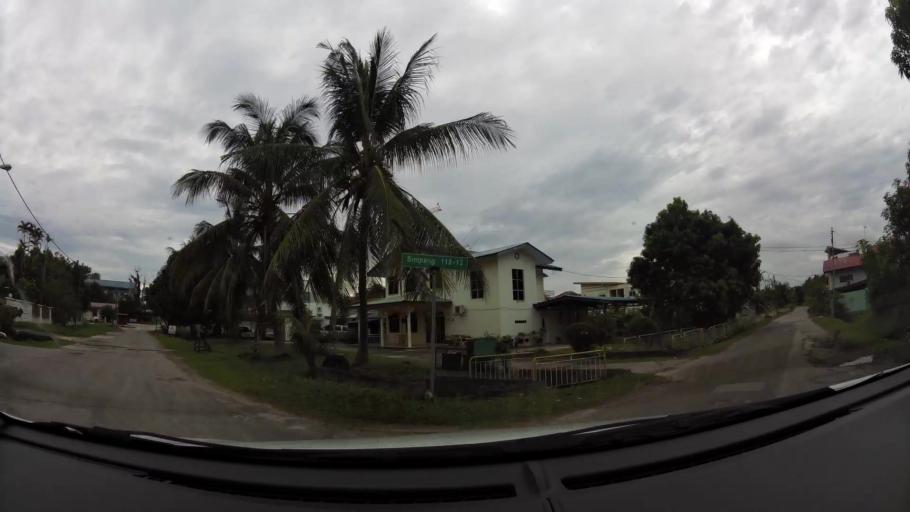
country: BN
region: Brunei and Muara
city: Bandar Seri Begawan
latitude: 4.8975
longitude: 114.9274
